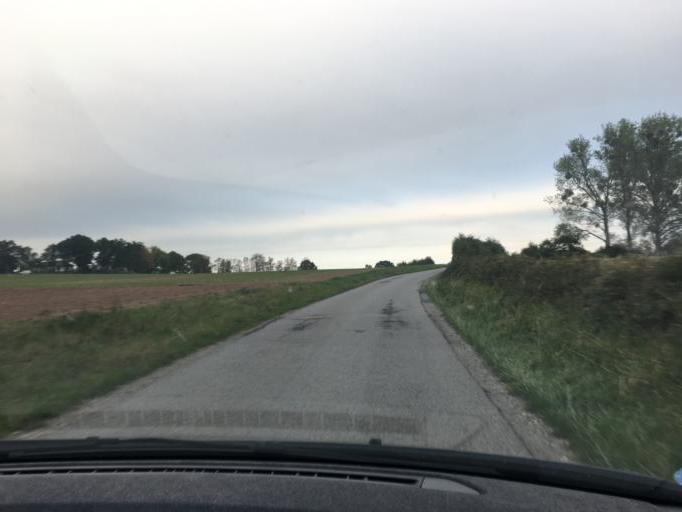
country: DE
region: North Rhine-Westphalia
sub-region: Regierungsbezirk Koln
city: Kreuzau
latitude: 50.7353
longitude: 6.4605
